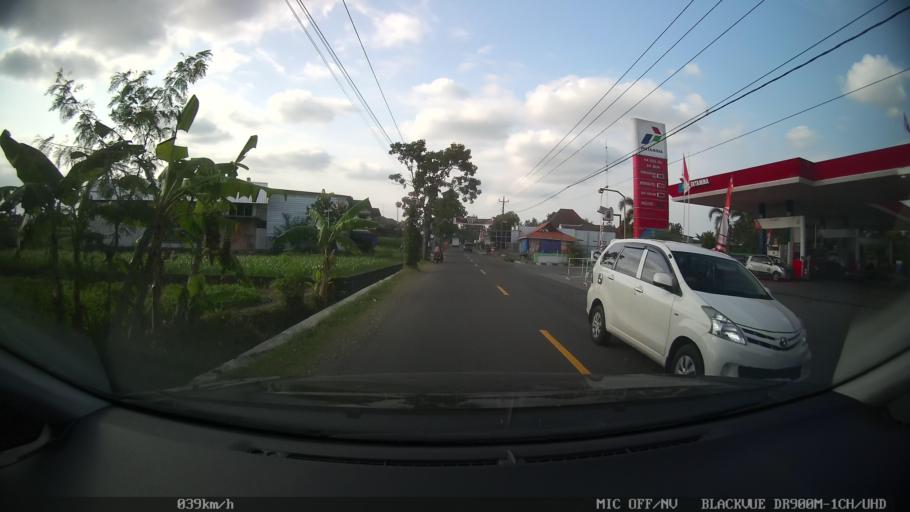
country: ID
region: Central Java
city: Candi Prambanan
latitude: -7.7221
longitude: 110.4724
